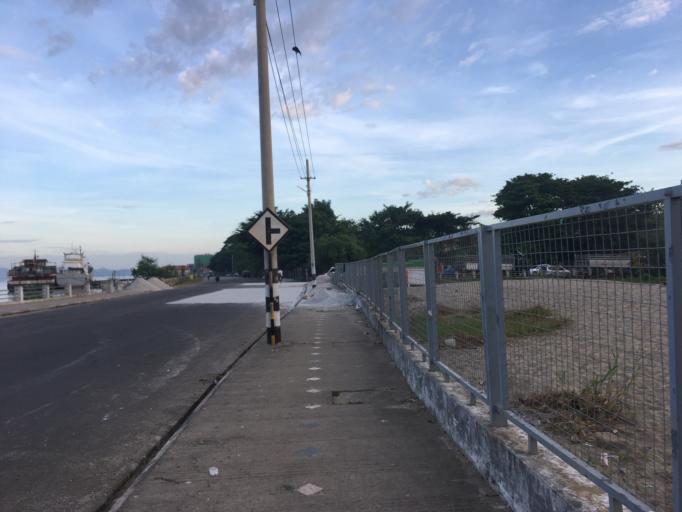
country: MM
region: Mon
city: Mawlamyine
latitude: 16.4637
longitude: 97.6225
